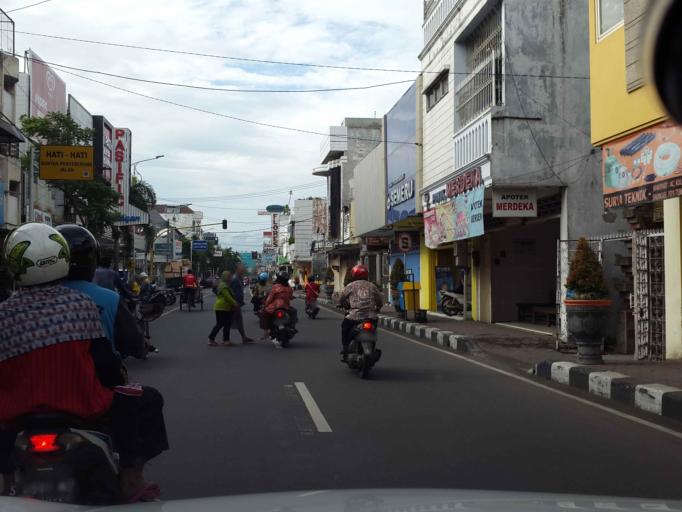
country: ID
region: East Java
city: Mojokerto
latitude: -7.4673
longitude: 112.4319
